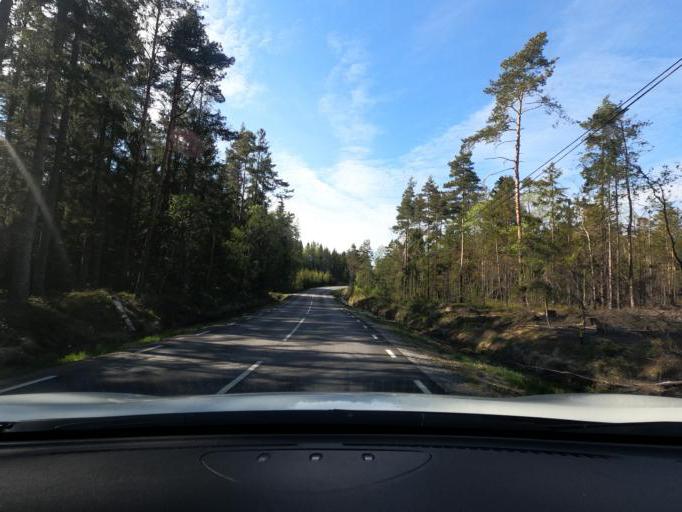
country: SE
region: Vaestra Goetaland
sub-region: Harryda Kommun
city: Landvetter
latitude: 57.6260
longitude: 12.2770
